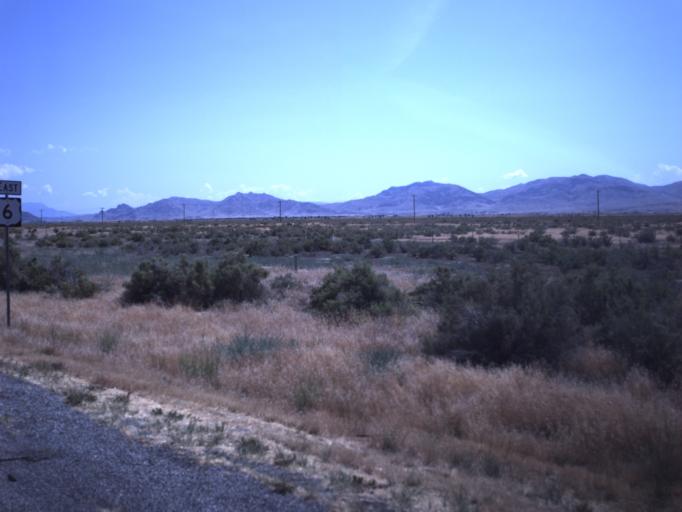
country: US
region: Utah
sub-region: Millard County
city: Delta
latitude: 39.4620
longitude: -112.4329
